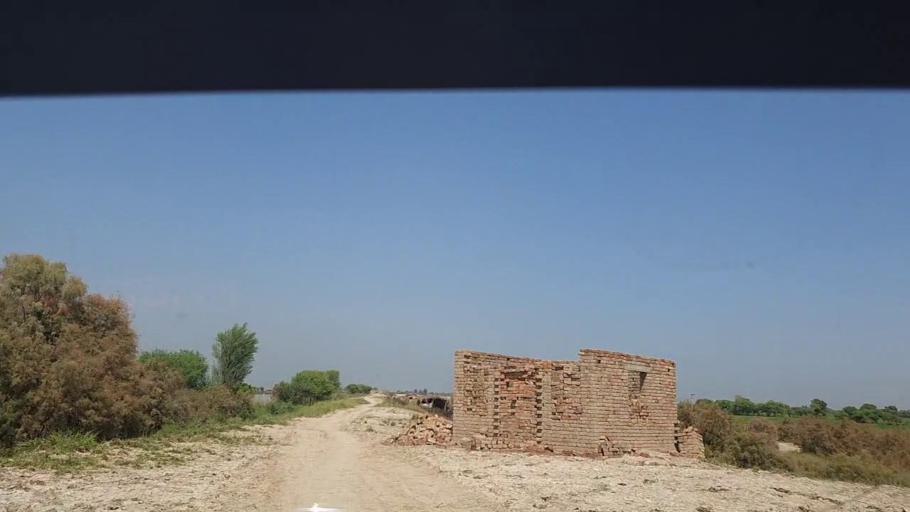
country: PK
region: Sindh
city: Kandhkot
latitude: 28.1845
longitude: 69.1572
